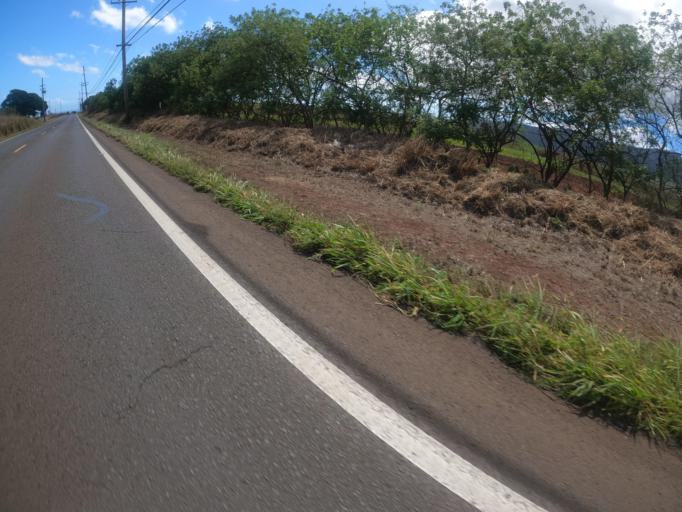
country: US
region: Hawaii
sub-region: Honolulu County
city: Village Park
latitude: 21.4213
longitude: -158.0506
